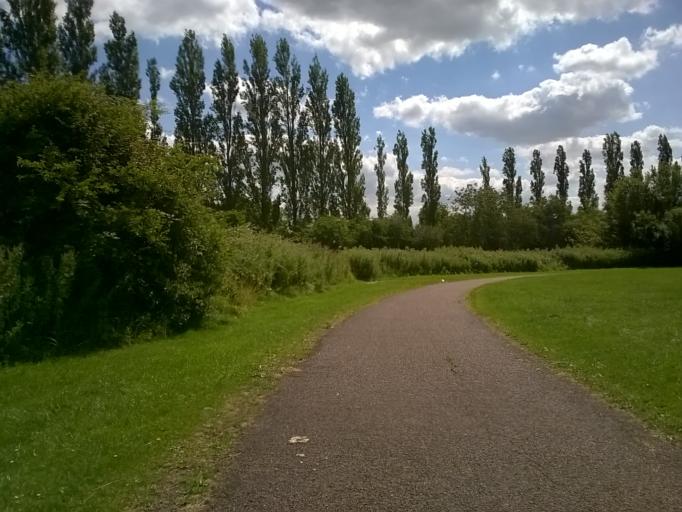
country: GB
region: England
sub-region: Milton Keynes
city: Milton Keynes
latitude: 52.0678
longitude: -0.7455
